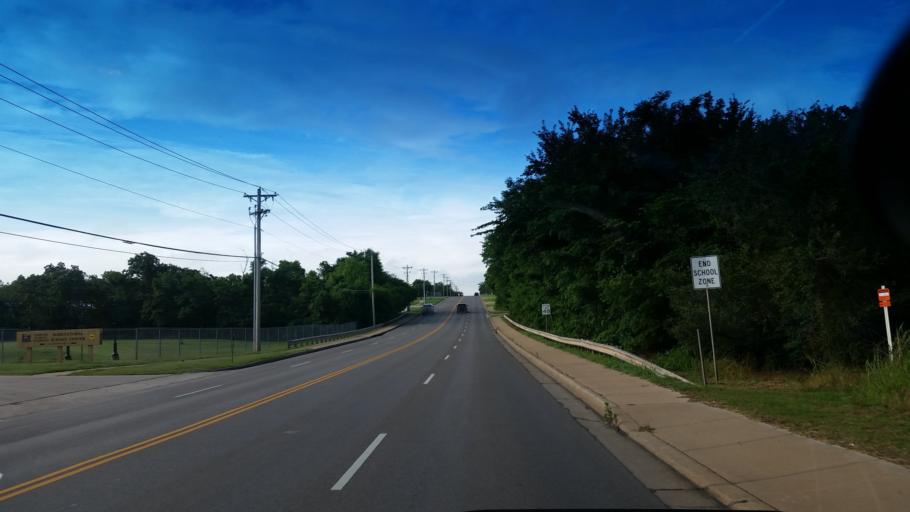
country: US
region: Oklahoma
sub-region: Oklahoma County
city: Edmond
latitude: 35.6600
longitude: -97.4961
